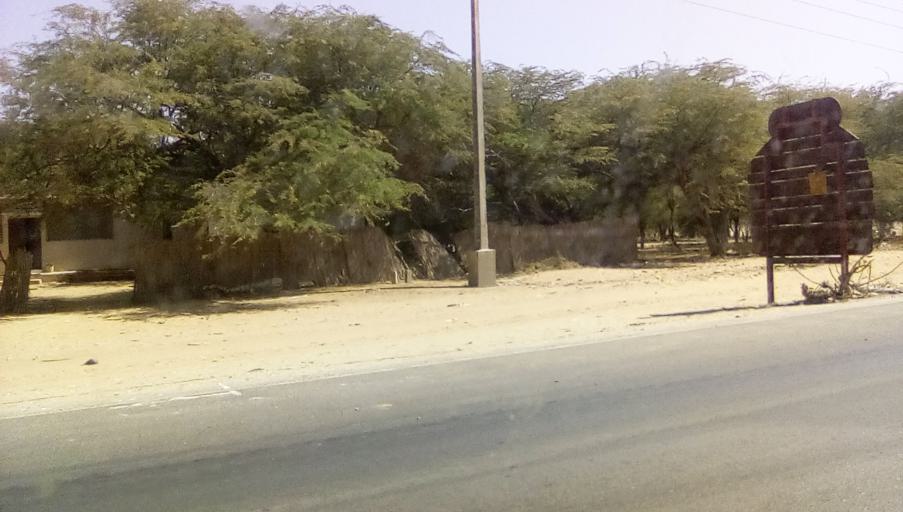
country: SN
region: Saint-Louis
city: Saint-Louis
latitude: 16.0398
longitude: -16.4480
